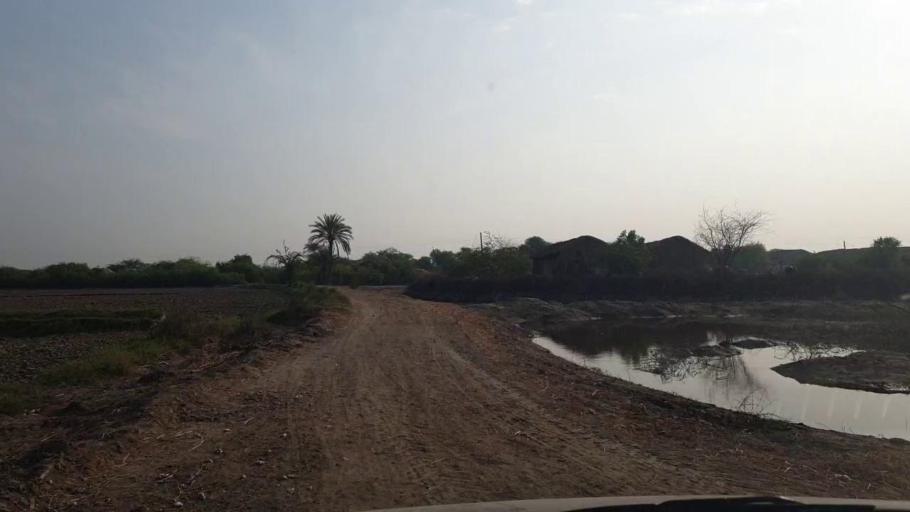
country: PK
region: Sindh
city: Tando Bago
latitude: 24.8034
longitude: 68.8828
